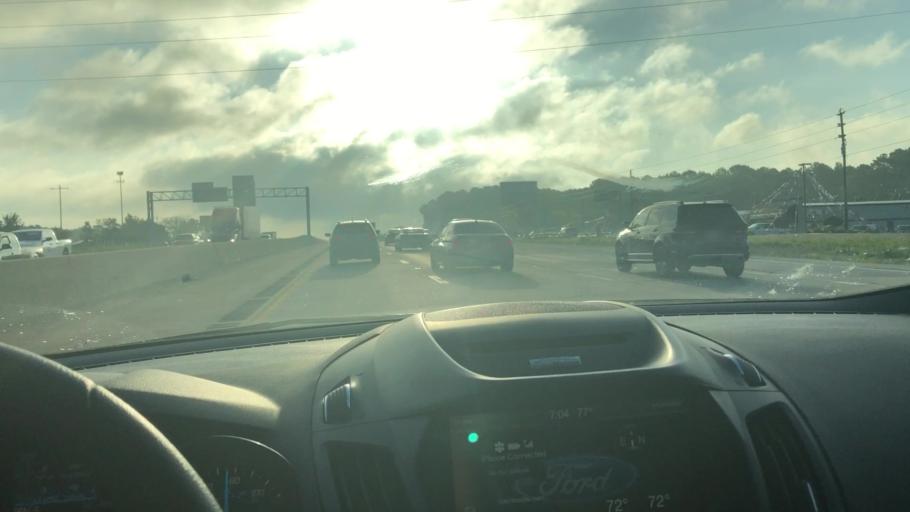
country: US
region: Arkansas
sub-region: Pulaski County
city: Alexander
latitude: 34.6339
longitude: -92.4629
